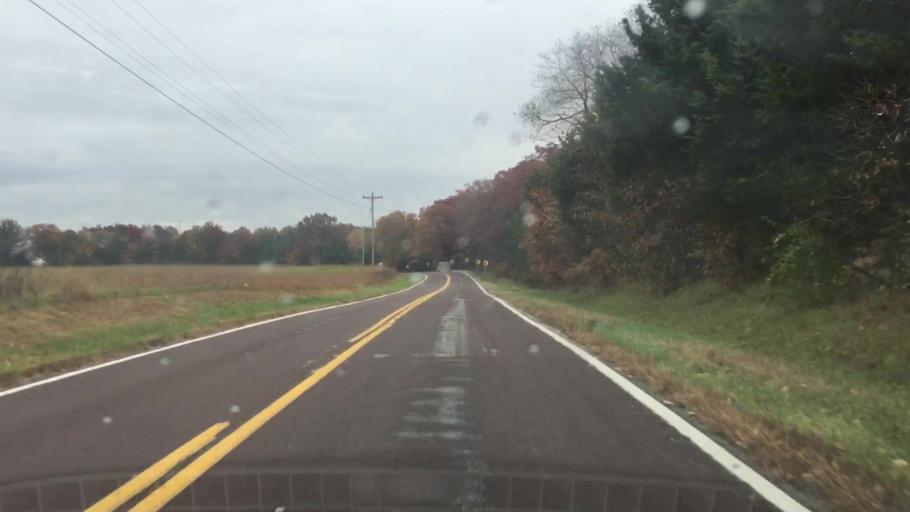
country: US
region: Missouri
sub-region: Callaway County
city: Fulton
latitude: 38.7826
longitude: -91.8167
